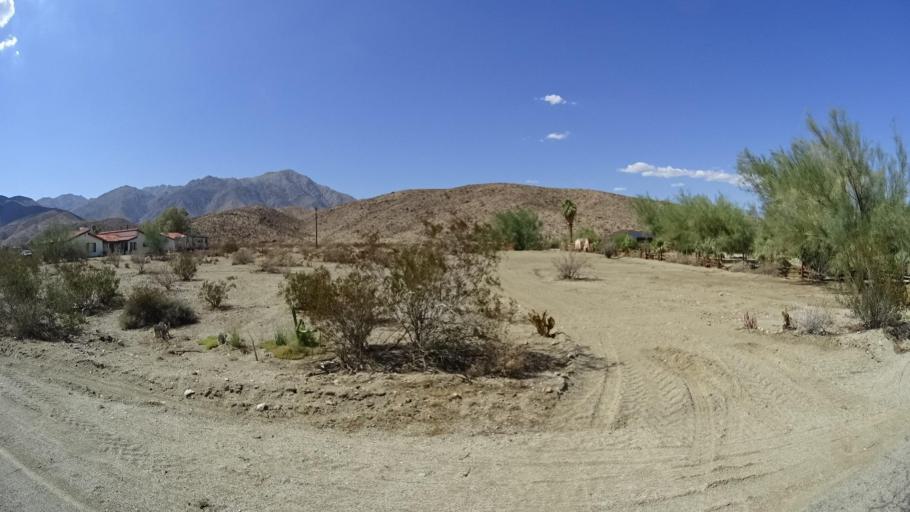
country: US
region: California
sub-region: San Diego County
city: Borrego Springs
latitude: 33.2415
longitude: -116.3810
